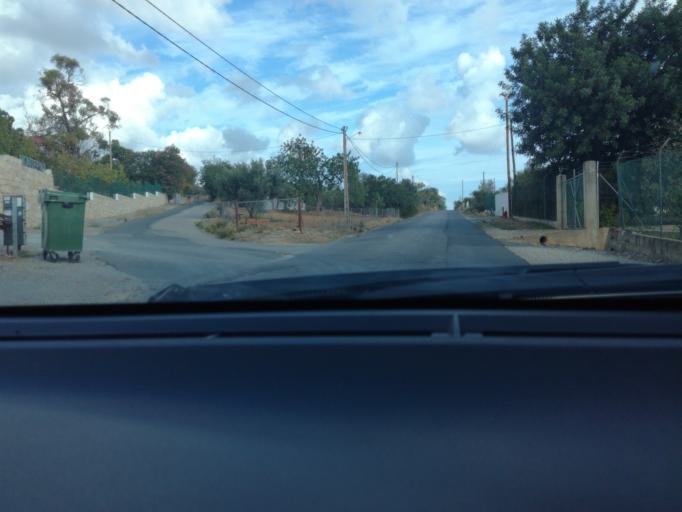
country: PT
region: Faro
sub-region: Olhao
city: Olhao
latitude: 37.0846
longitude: -7.8755
